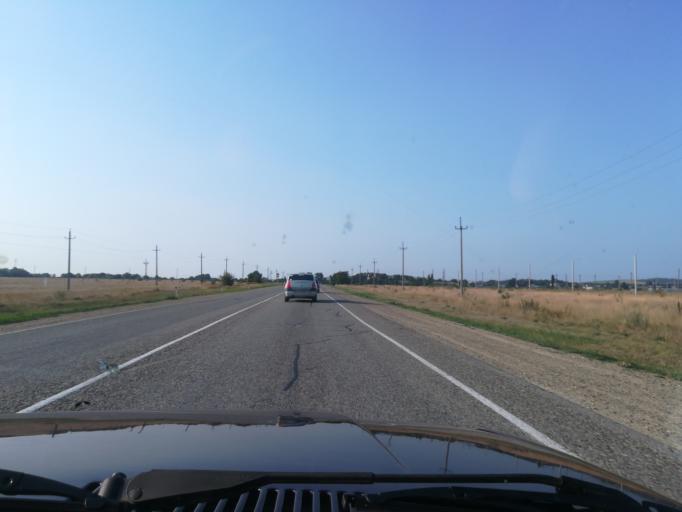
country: RU
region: Krasnodarskiy
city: Yurovka
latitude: 45.1054
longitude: 37.4220
